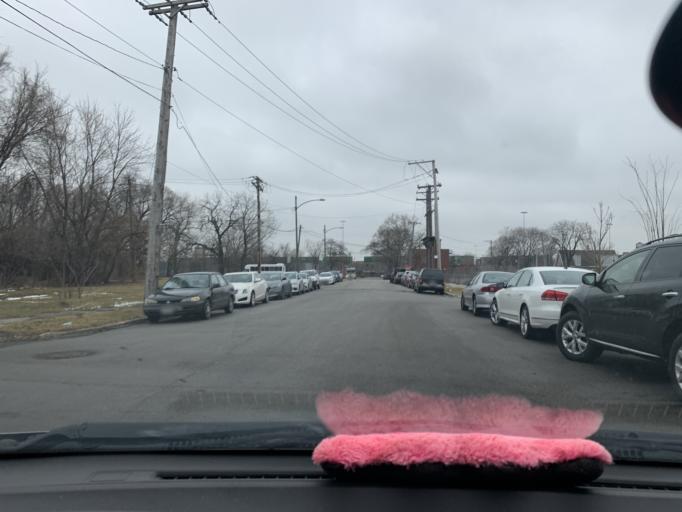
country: US
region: Illinois
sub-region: Cook County
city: Chicago
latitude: 41.8656
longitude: -87.6834
